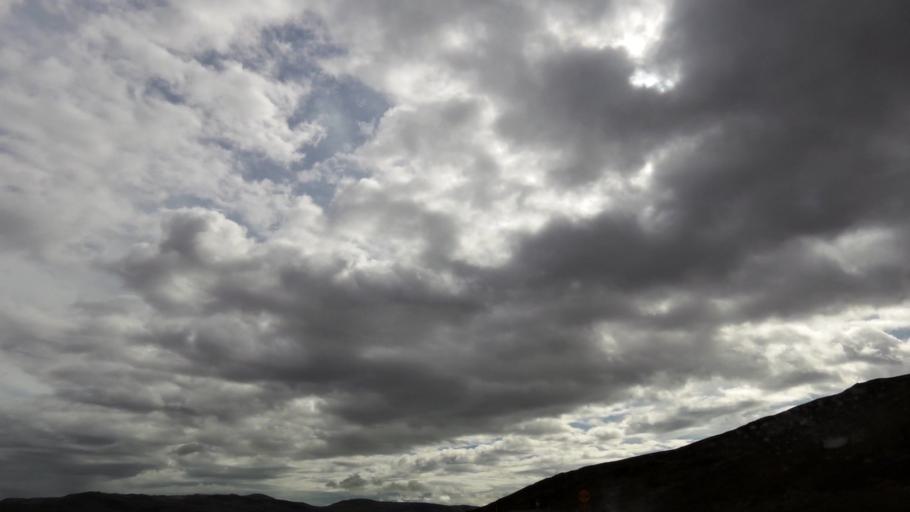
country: IS
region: West
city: Stykkisholmur
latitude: 65.5853
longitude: -22.1556
